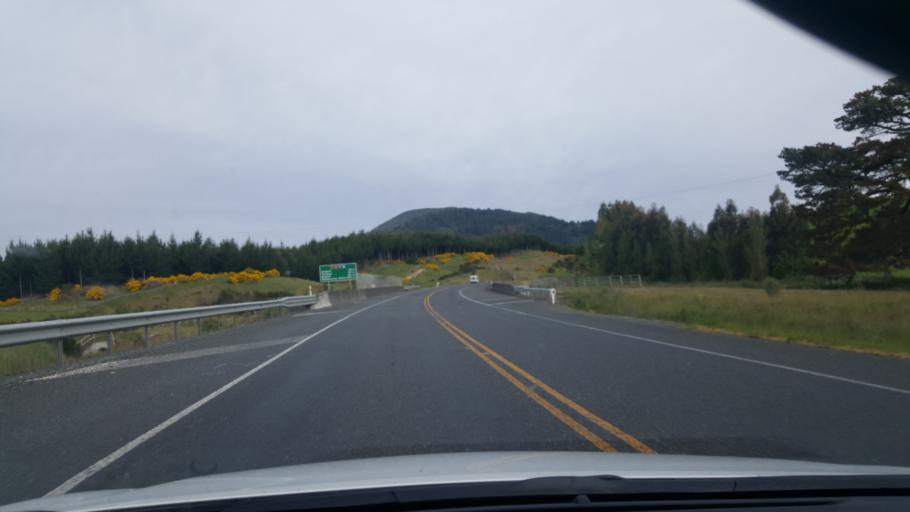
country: NZ
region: Waikato
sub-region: Taupo District
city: Taupo
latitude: -38.6706
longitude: 176.1115
